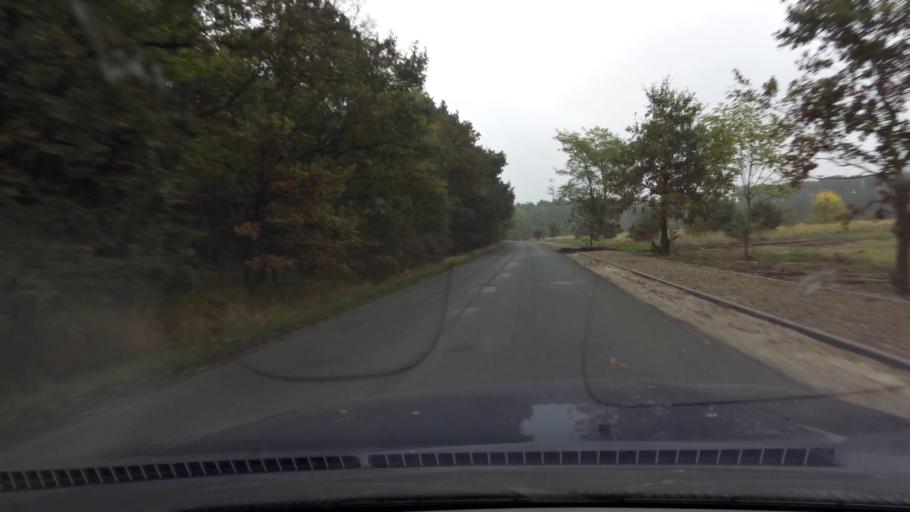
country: PL
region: West Pomeranian Voivodeship
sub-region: Powiat goleniowski
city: Goleniow
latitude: 53.5267
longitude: 14.7564
